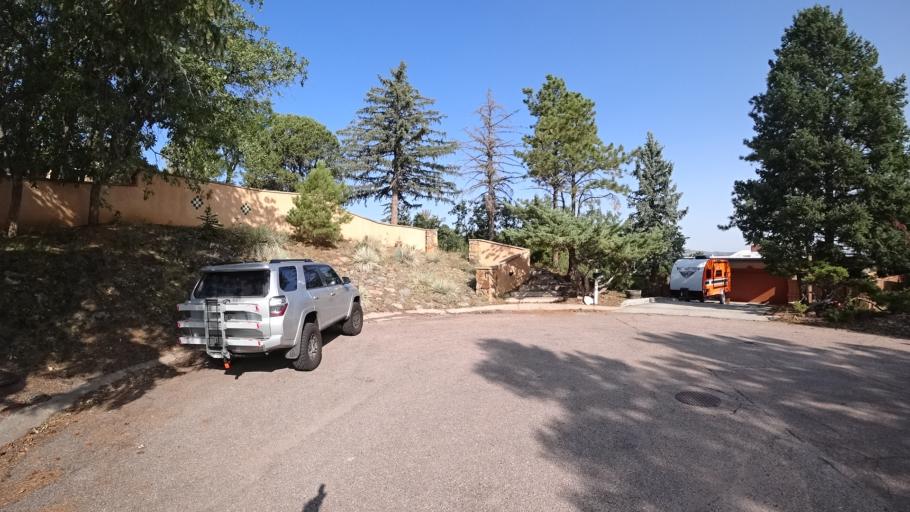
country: US
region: Colorado
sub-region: El Paso County
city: Colorado Springs
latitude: 38.8169
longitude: -104.8678
